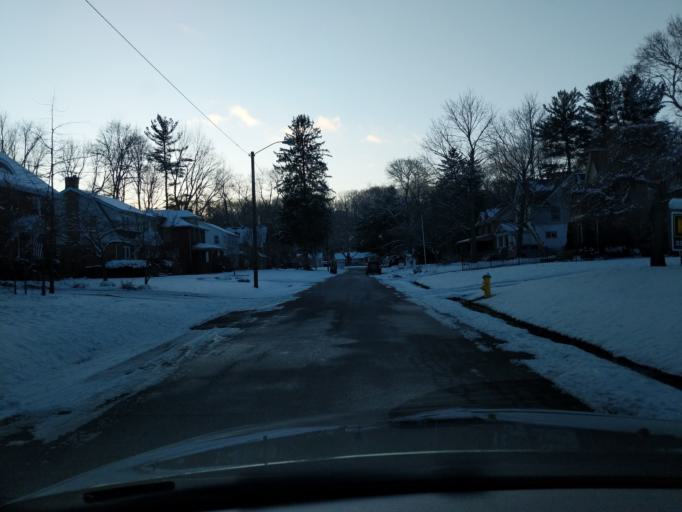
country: US
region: Ohio
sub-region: Summit County
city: Fairlawn
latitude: 41.1114
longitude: -81.5830
